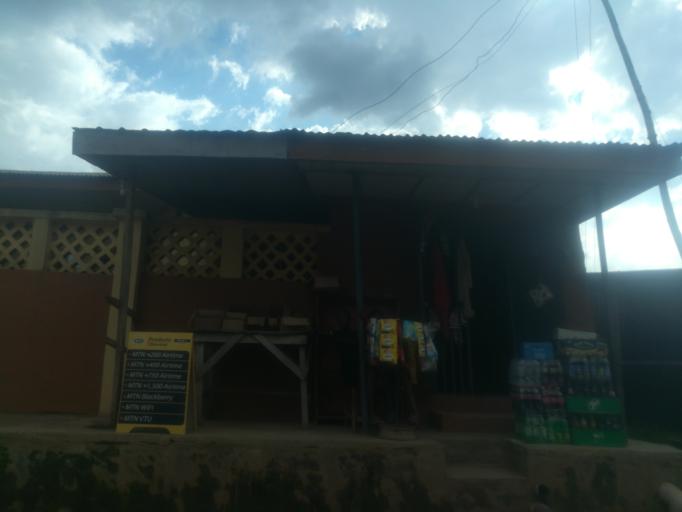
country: NG
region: Oyo
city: Ibadan
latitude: 7.4073
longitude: 3.8290
